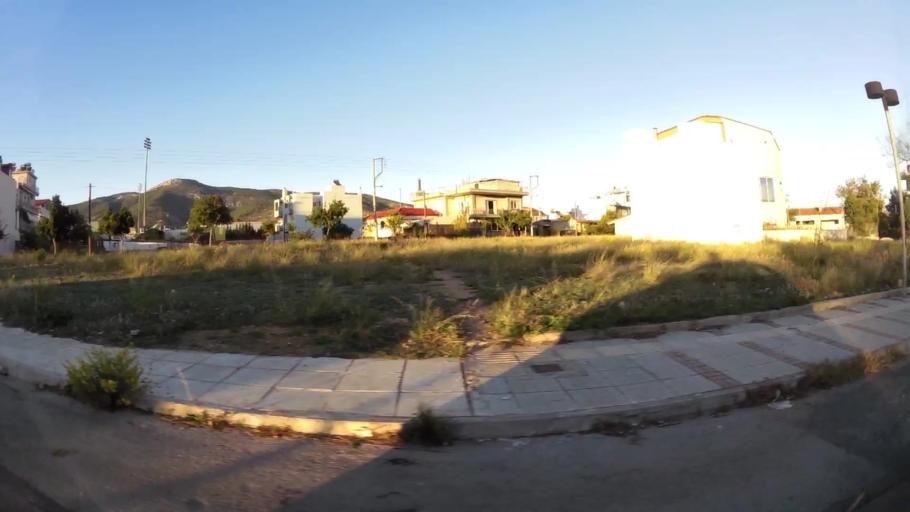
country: GR
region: Attica
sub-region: Nomarchia Dytikis Attikis
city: Ano Liosia
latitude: 38.0830
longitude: 23.6891
